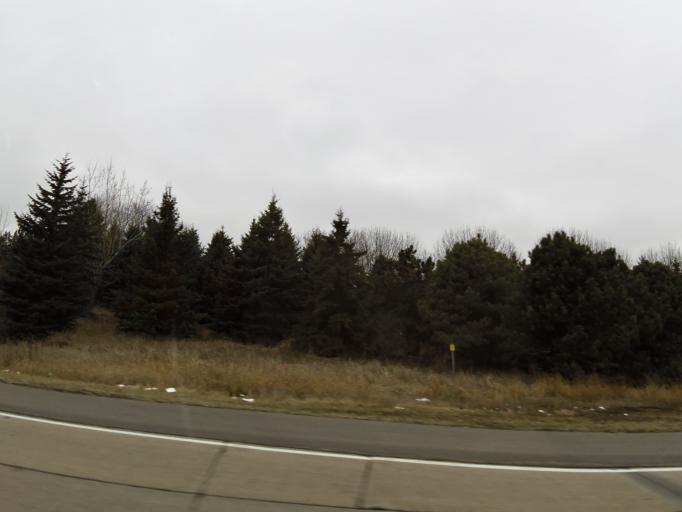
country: US
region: Minnesota
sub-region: Dakota County
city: Eagan
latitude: 44.7838
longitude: -93.2091
